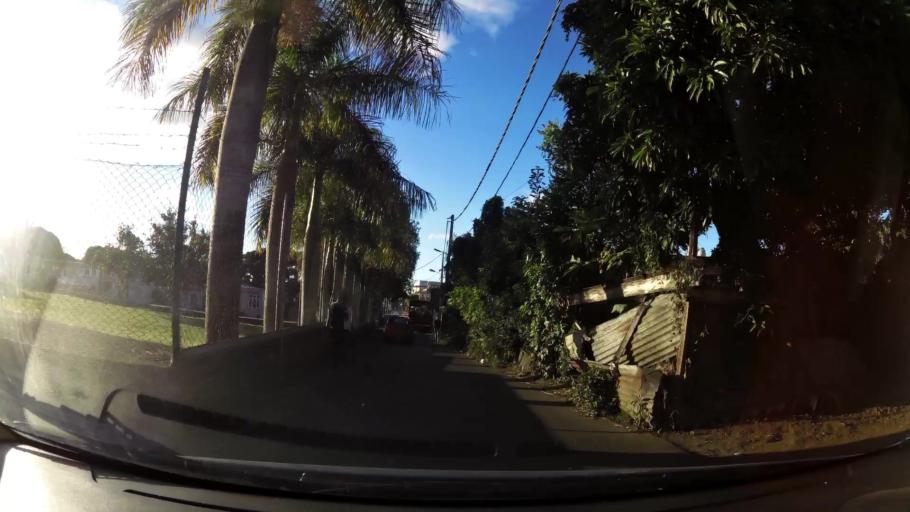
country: MU
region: Plaines Wilhems
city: Quatre Bornes
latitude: -20.2513
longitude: 57.4617
